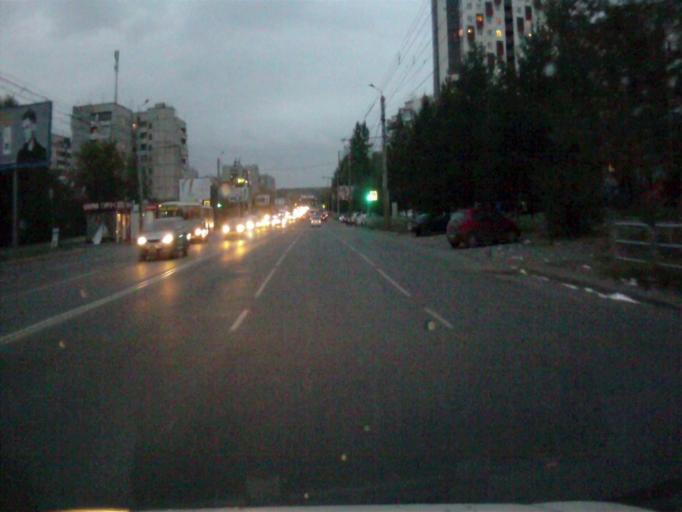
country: RU
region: Chelyabinsk
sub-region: Gorod Chelyabinsk
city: Chelyabinsk
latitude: 55.1836
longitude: 61.3326
